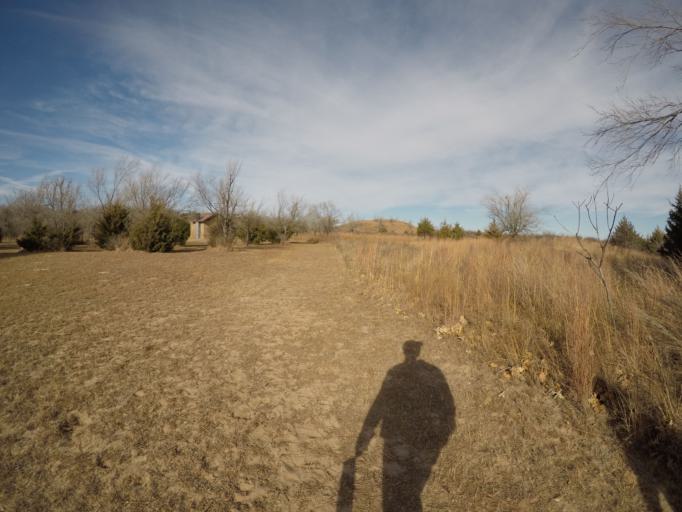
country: US
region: Kansas
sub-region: Reno County
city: Buhler
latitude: 38.1164
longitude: -97.8566
